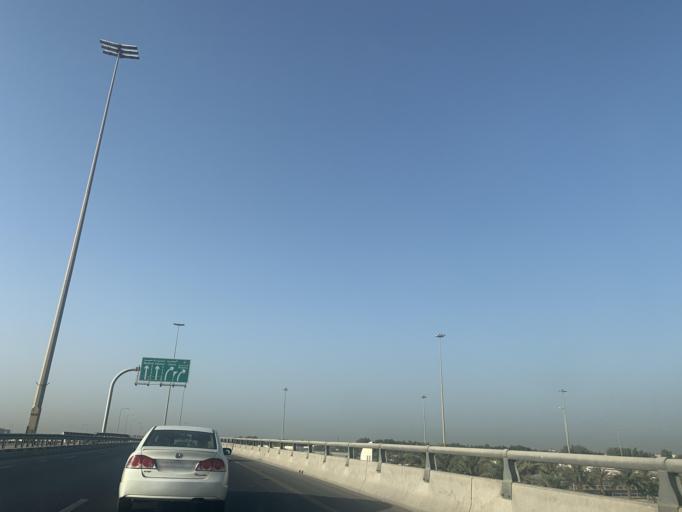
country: BH
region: Central Governorate
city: Madinat Hamad
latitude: 26.1738
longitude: 50.4653
